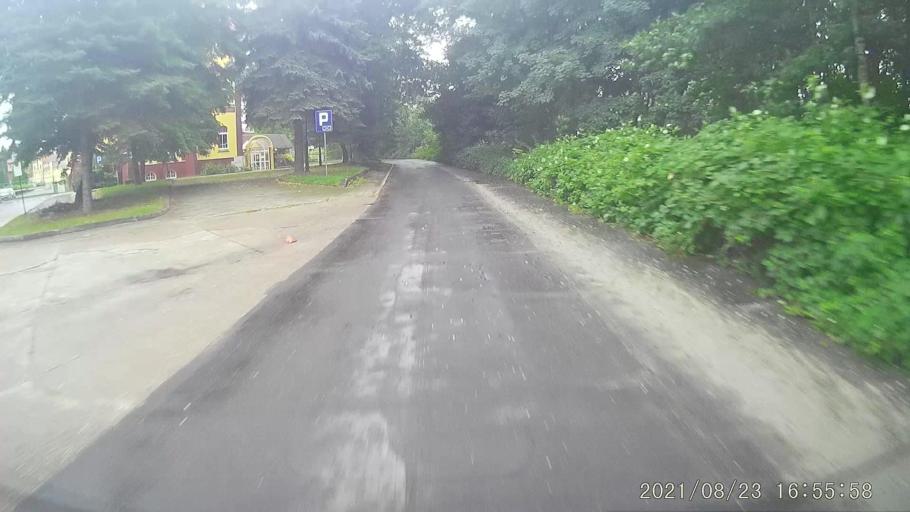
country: PL
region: Lower Silesian Voivodeship
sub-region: Powiat zgorzelecki
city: Zgorzelec
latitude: 51.1680
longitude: 15.0126
